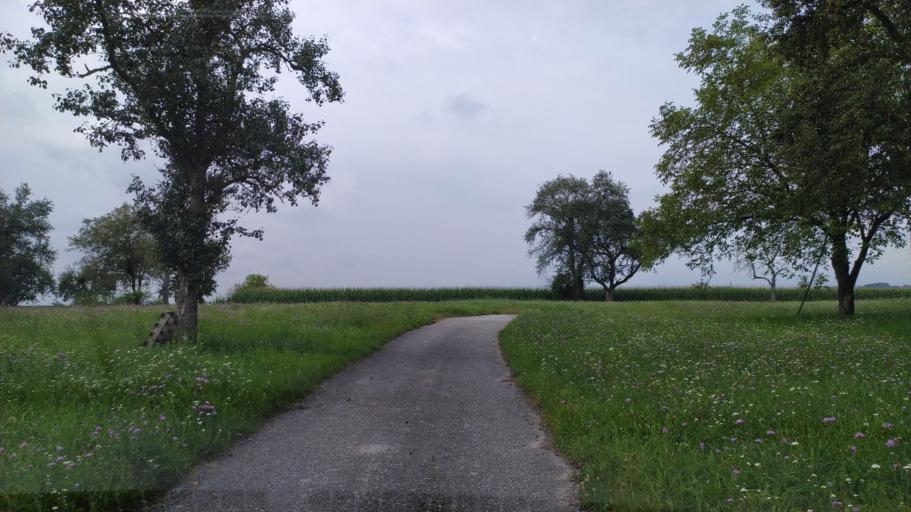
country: AT
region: Upper Austria
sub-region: Politischer Bezirk Perg
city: Bad Kreuzen
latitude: 48.1995
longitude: 14.7871
